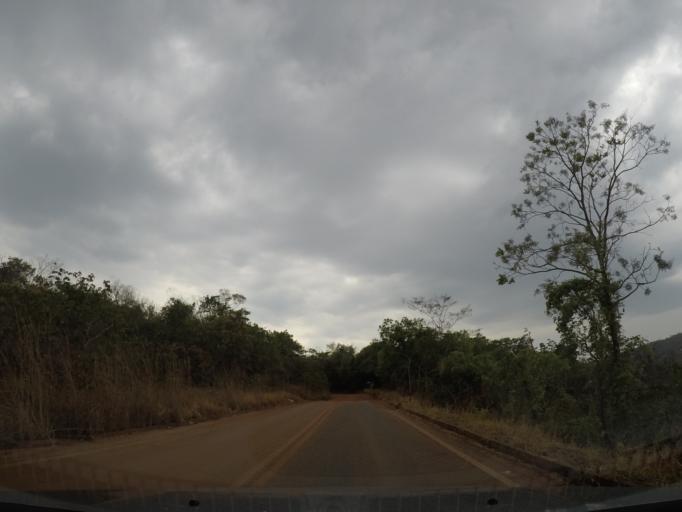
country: BR
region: Goias
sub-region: Pirenopolis
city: Pirenopolis
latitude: -15.8440
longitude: -48.9173
